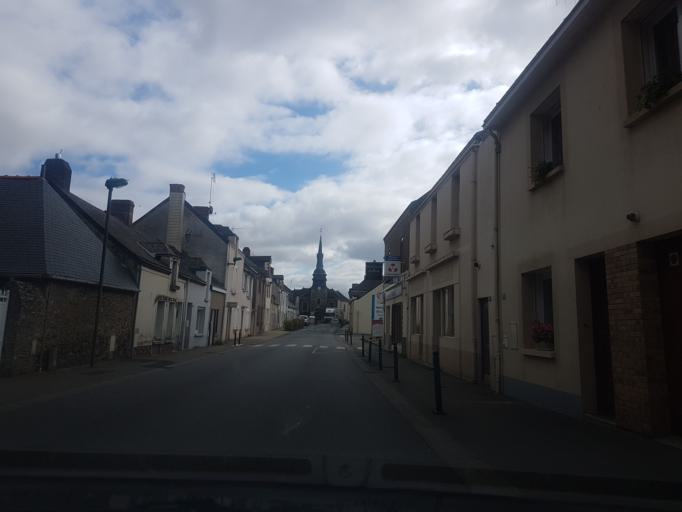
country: FR
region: Pays de la Loire
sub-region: Departement de la Loire-Atlantique
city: Ligne
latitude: 47.4124
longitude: -1.3792
